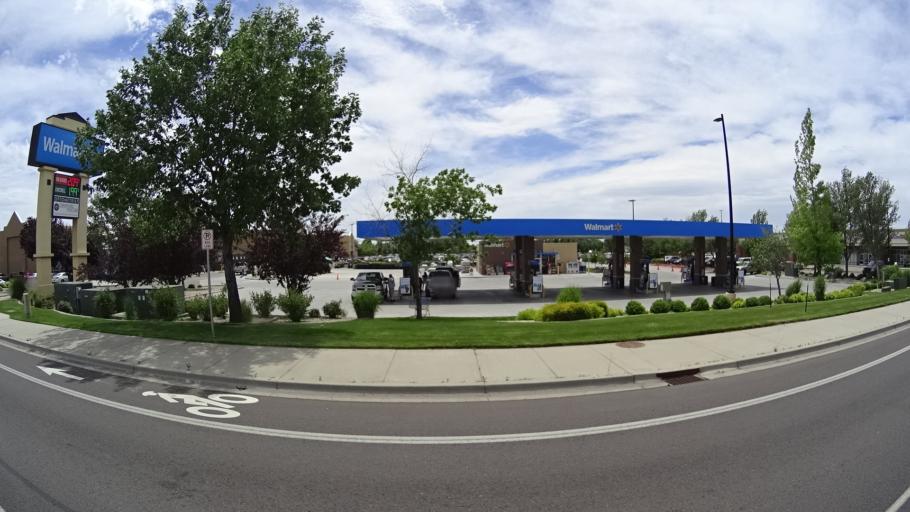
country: US
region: Idaho
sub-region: Ada County
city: Meridian
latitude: 43.6194
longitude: -116.3449
